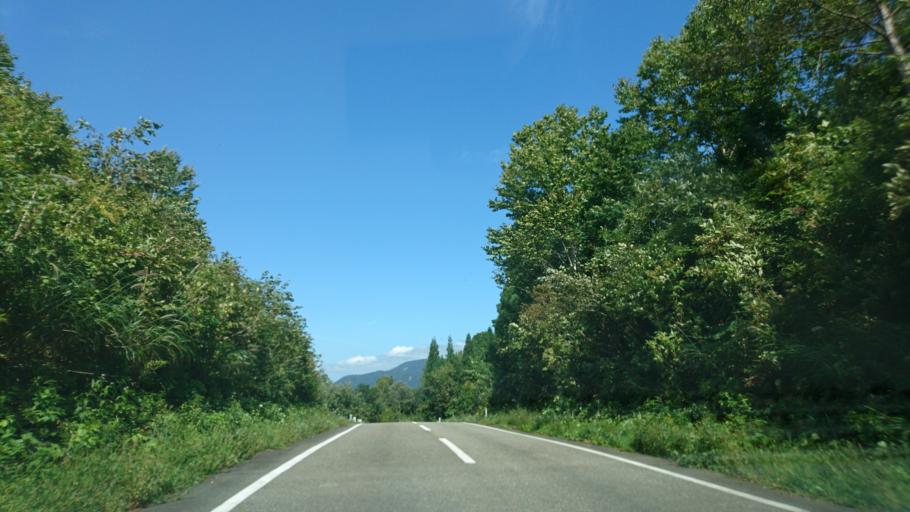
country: JP
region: Akita
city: Yuzawa
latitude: 38.9595
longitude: 140.7135
